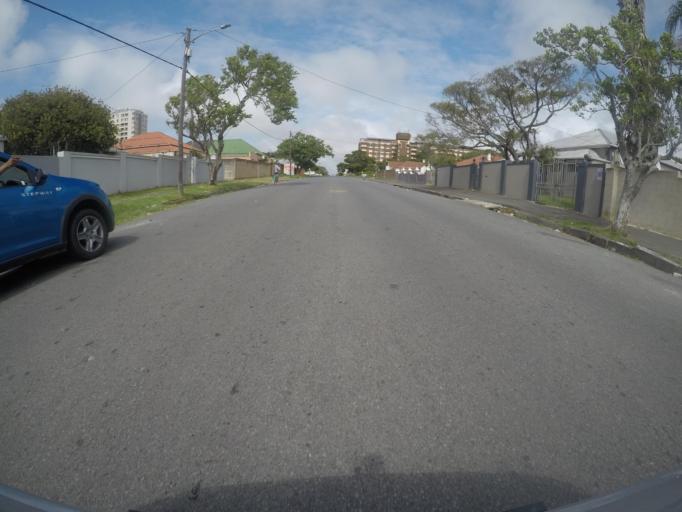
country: ZA
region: Eastern Cape
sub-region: Buffalo City Metropolitan Municipality
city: East London
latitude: -32.9987
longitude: 27.9081
